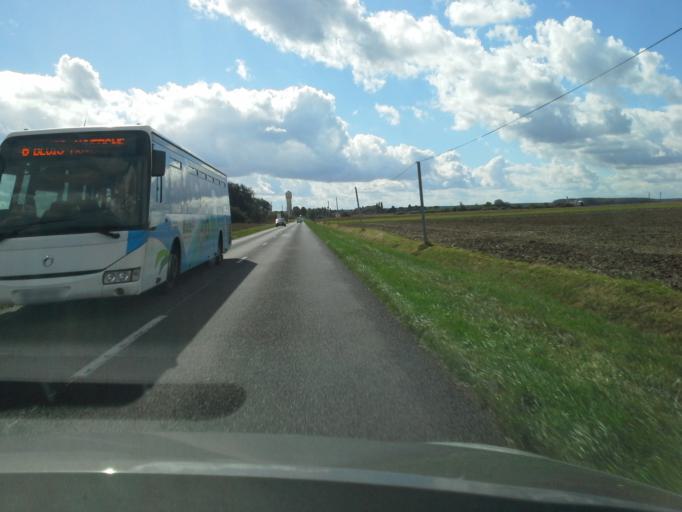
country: FR
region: Centre
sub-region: Departement du Loir-et-Cher
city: Pontlevoy
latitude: 47.4061
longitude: 1.2676
